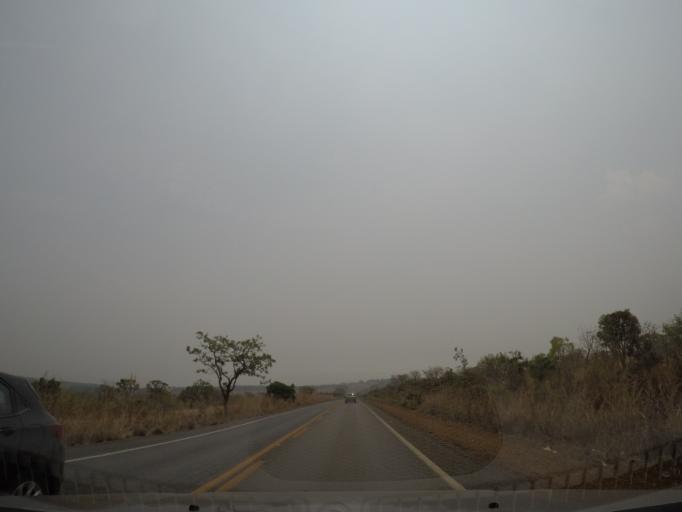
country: BR
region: Goias
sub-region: Pirenopolis
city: Pirenopolis
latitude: -15.8920
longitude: -48.8892
